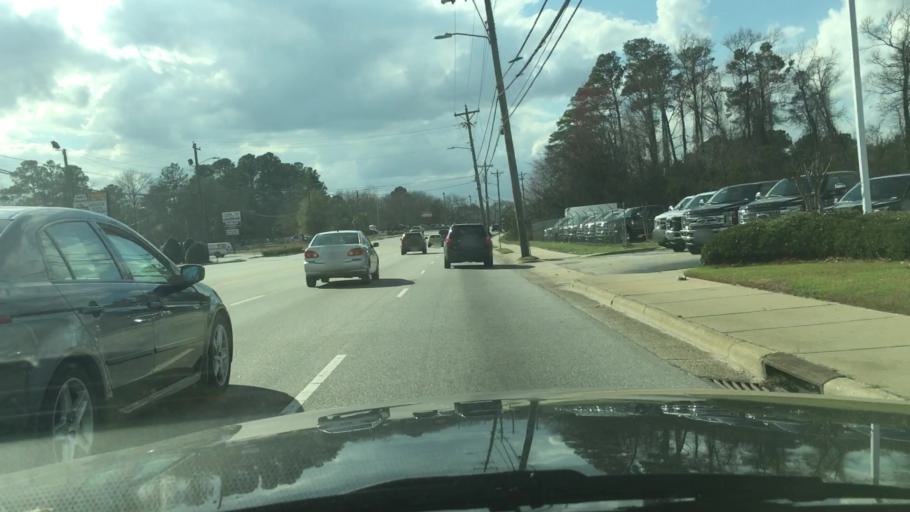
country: US
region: North Carolina
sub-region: Cumberland County
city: Hope Mills
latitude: 35.0426
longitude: -78.9651
